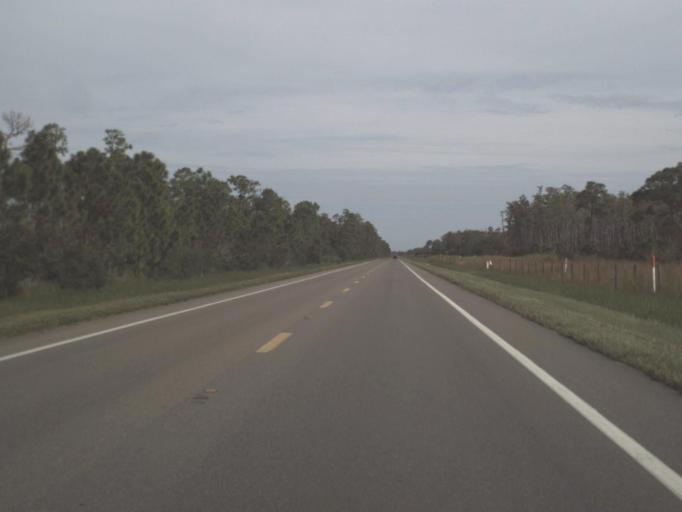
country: US
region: Florida
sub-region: Lee County
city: Olga
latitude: 26.9206
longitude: -81.7605
